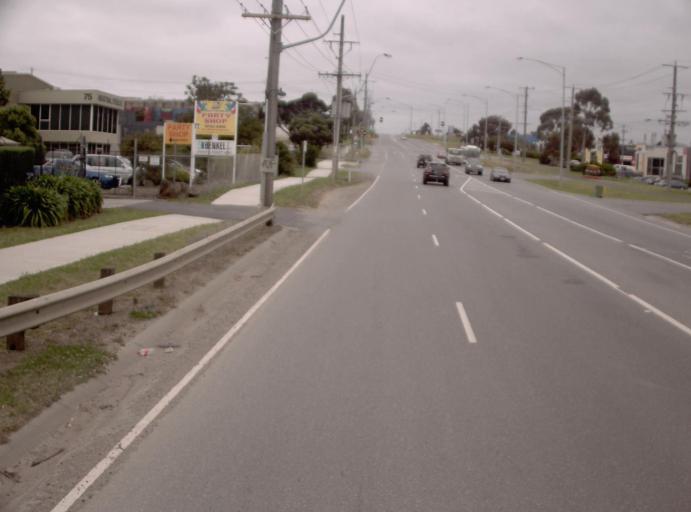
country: AU
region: Victoria
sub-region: Casey
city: Hallam
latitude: -38.0172
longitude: 145.2709
